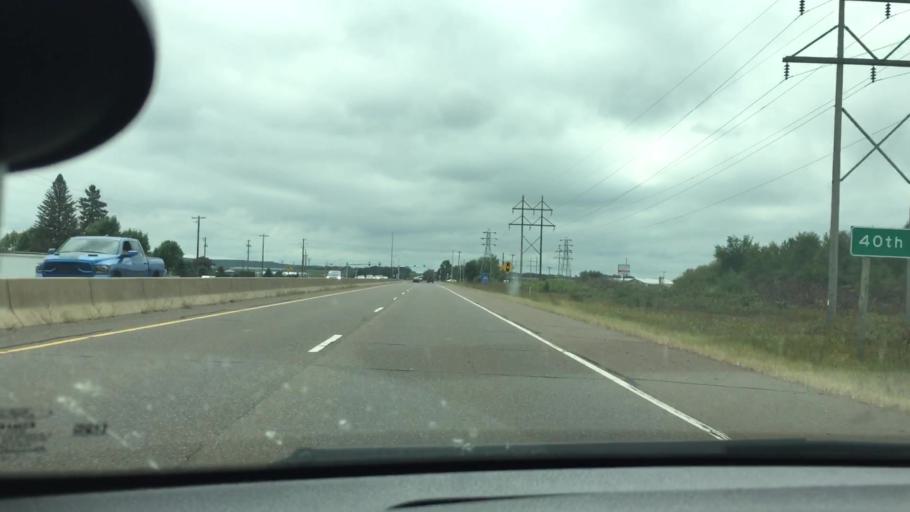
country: US
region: Wisconsin
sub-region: Chippewa County
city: Chippewa Falls
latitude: 44.9033
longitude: -91.4116
